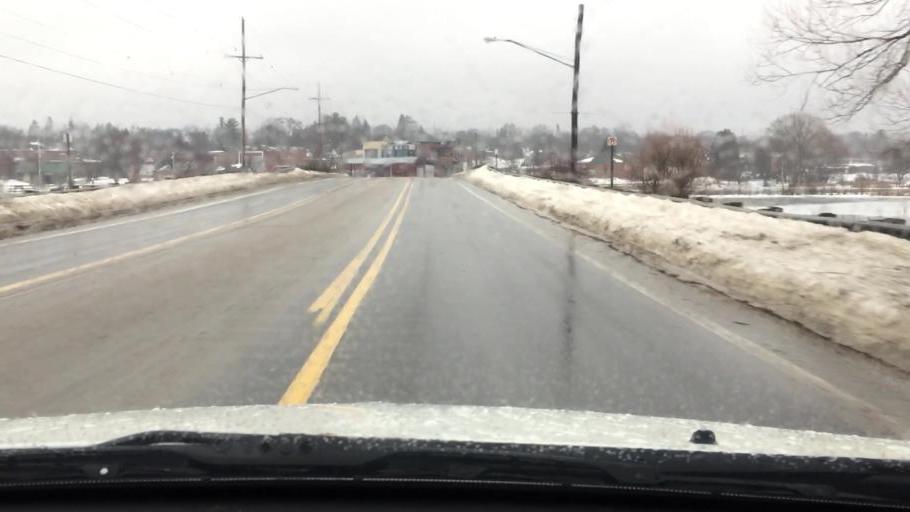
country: US
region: Michigan
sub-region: Charlevoix County
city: East Jordan
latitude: 45.1533
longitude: -85.1307
